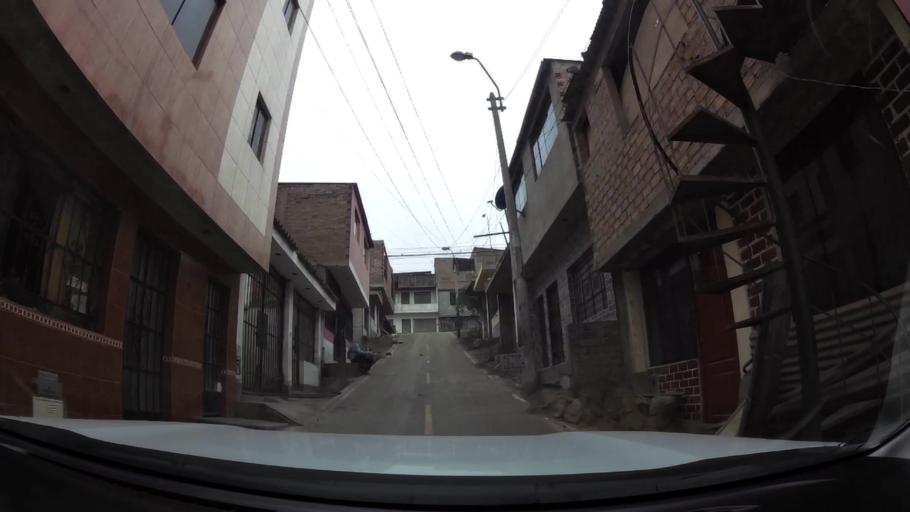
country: PE
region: Lima
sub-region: Lima
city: Surco
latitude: -12.1684
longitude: -76.9587
